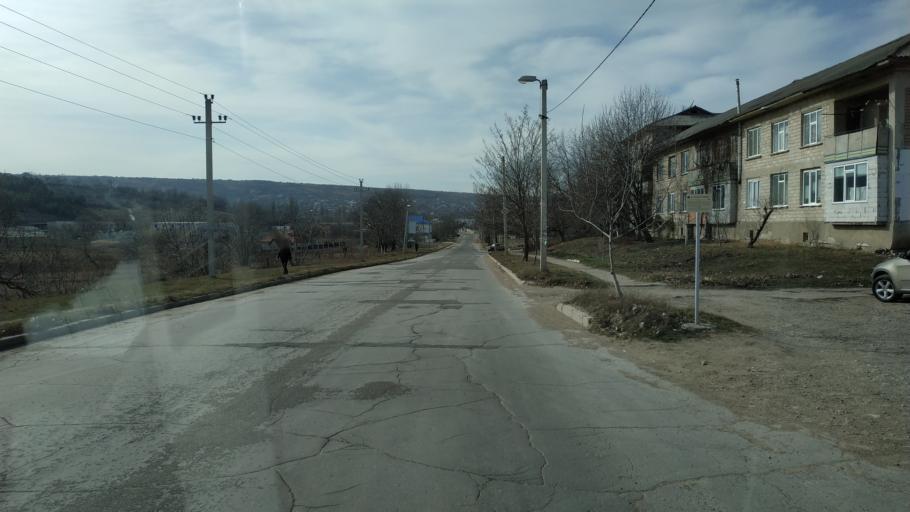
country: MD
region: Chisinau
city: Vatra
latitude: 47.0724
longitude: 28.6963
